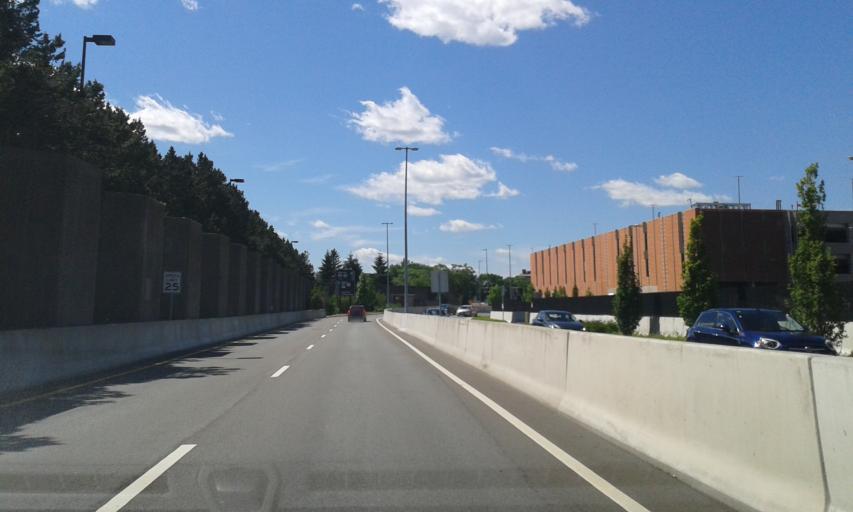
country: US
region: Massachusetts
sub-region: Suffolk County
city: Chelsea
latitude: 42.3662
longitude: -71.0294
